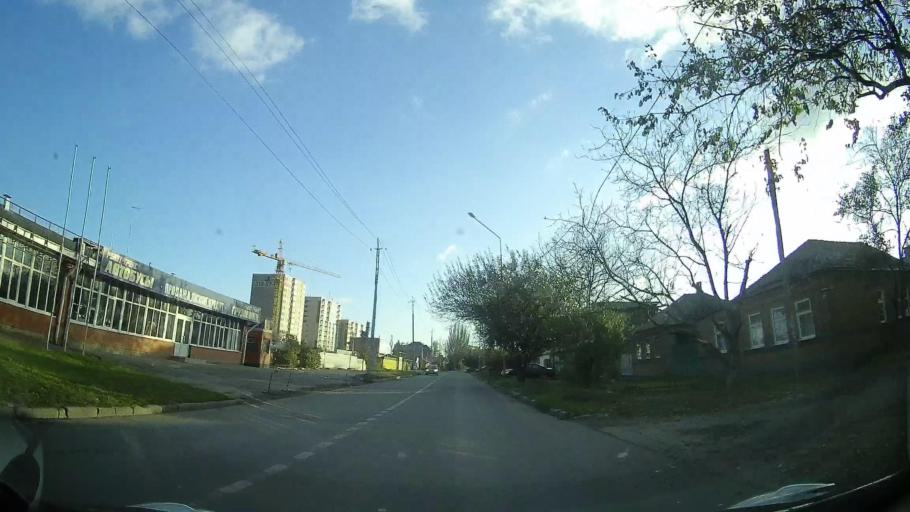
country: RU
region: Rostov
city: Imeni Chkalova
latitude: 47.2427
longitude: 39.7775
